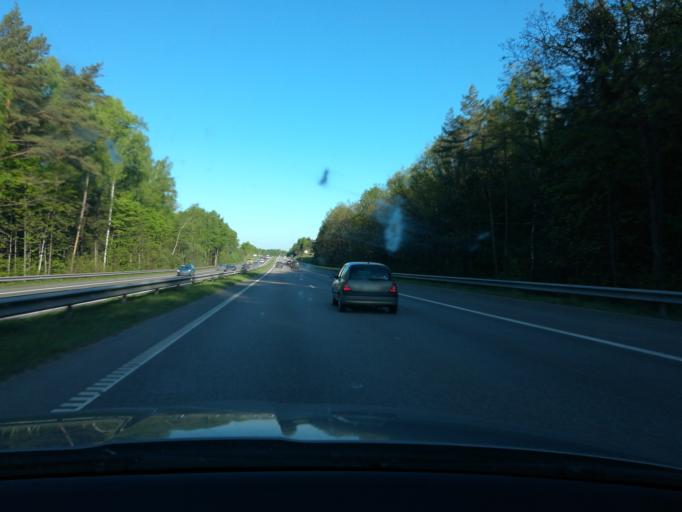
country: LT
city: Ziezmariai
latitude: 54.8010
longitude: 24.5216
